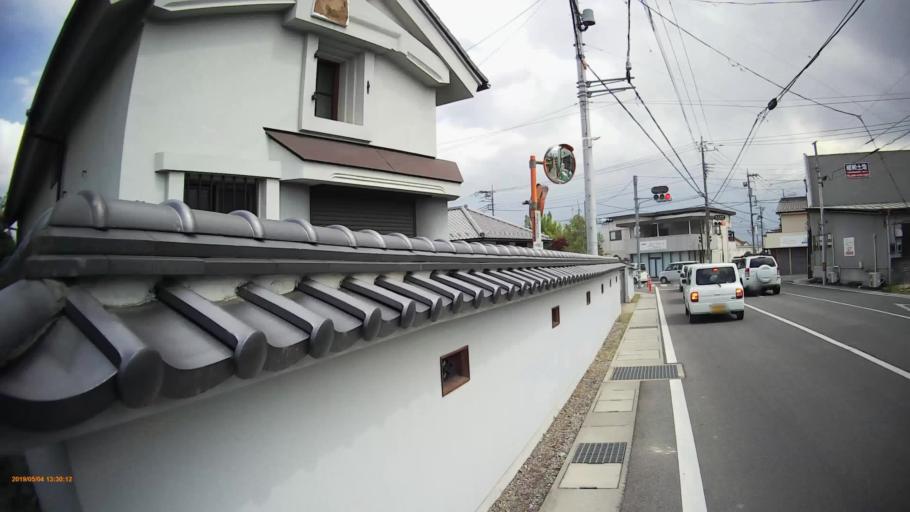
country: JP
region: Yamanashi
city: Ryuo
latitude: 35.6663
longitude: 138.5181
